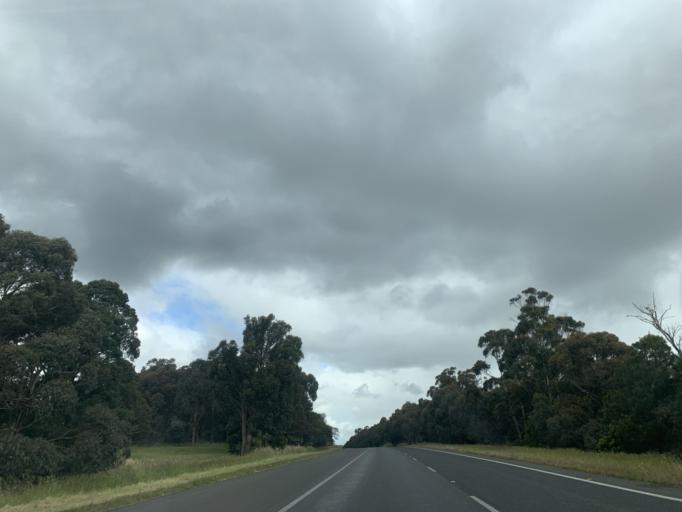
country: AU
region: Victoria
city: Black Hill
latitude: -37.5339
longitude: 143.8758
